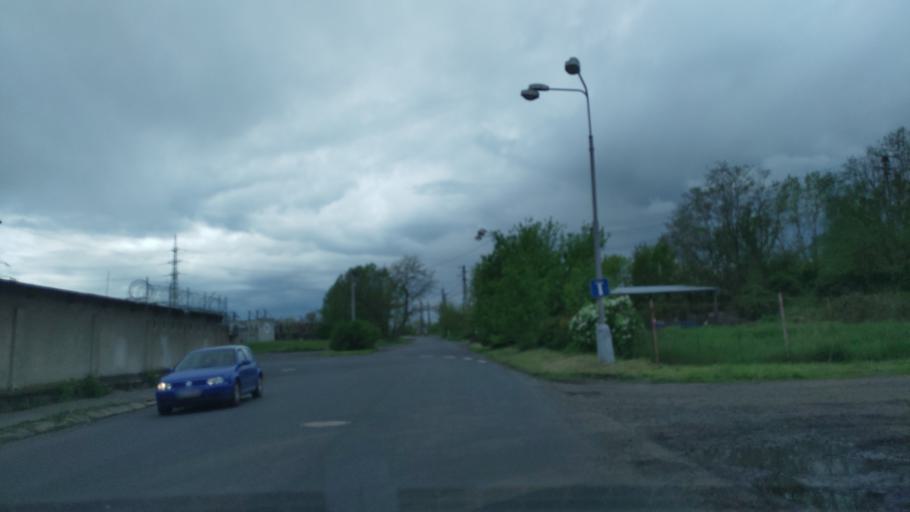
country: CZ
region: Ustecky
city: Trmice
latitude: 50.6460
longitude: 13.9843
